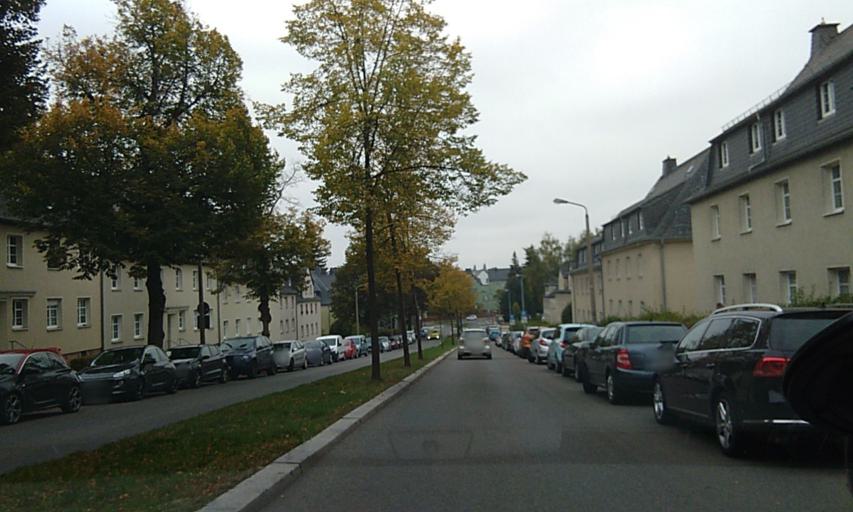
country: DE
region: Saxony
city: Chemnitz
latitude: 50.8411
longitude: 12.8870
